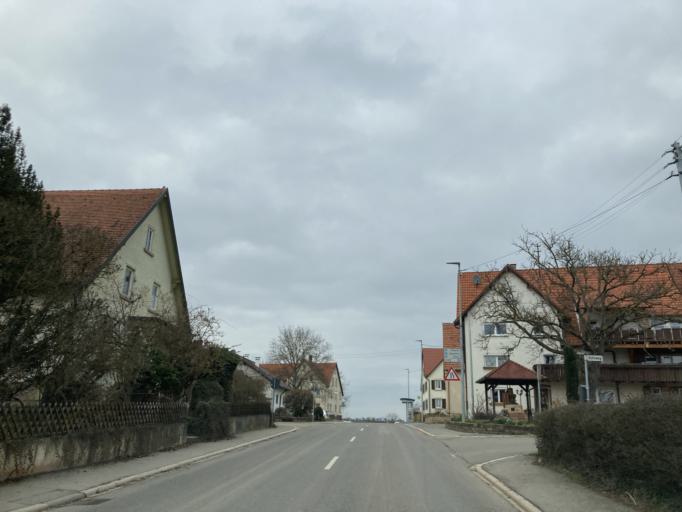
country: DE
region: Baden-Wuerttemberg
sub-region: Tuebingen Region
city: Hirrlingen
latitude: 48.4511
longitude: 8.8808
